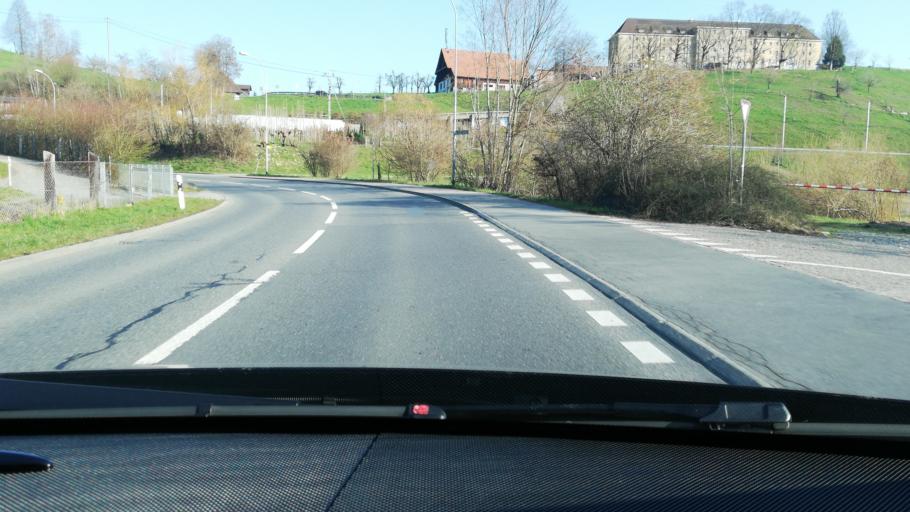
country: CH
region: Lucerne
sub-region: Lucerne-Stadt District
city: Luzern
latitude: 47.0631
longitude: 8.2982
